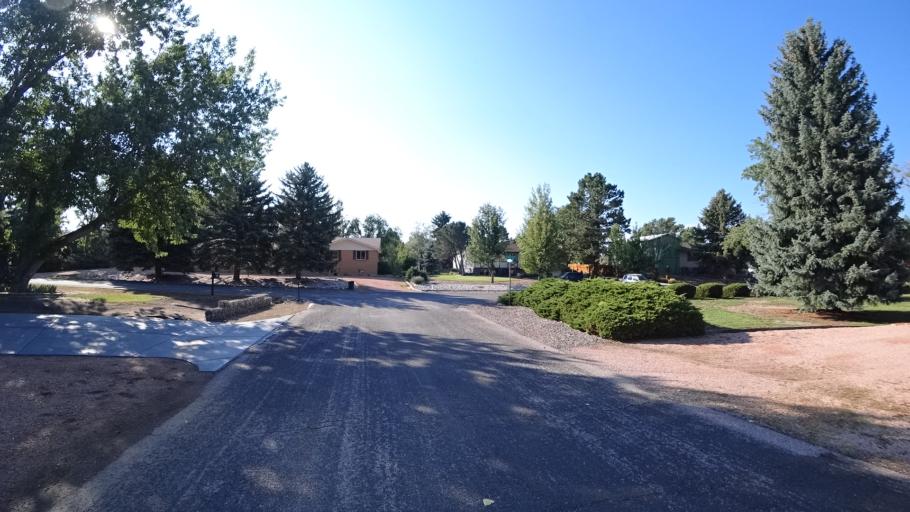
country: US
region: Colorado
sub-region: El Paso County
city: Air Force Academy
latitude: 38.9319
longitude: -104.7874
